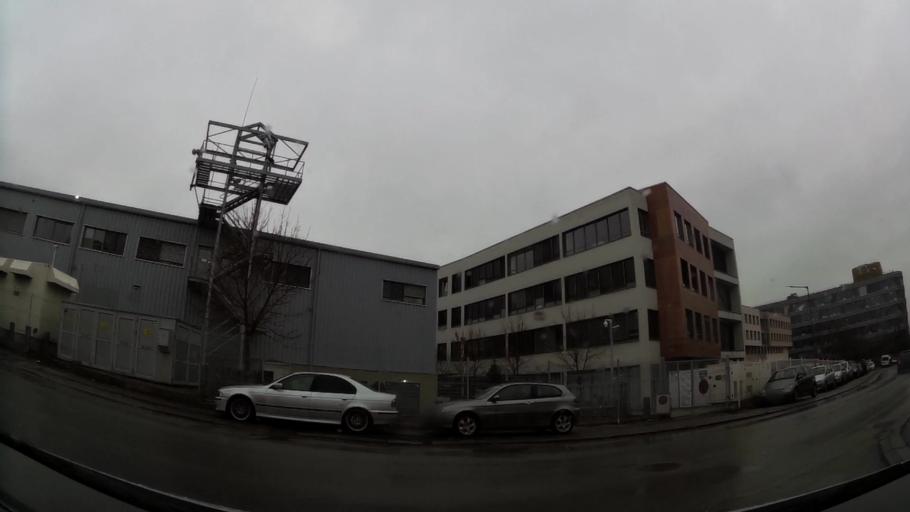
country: BG
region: Sofia-Capital
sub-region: Stolichna Obshtina
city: Sofia
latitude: 42.6253
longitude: 23.3783
